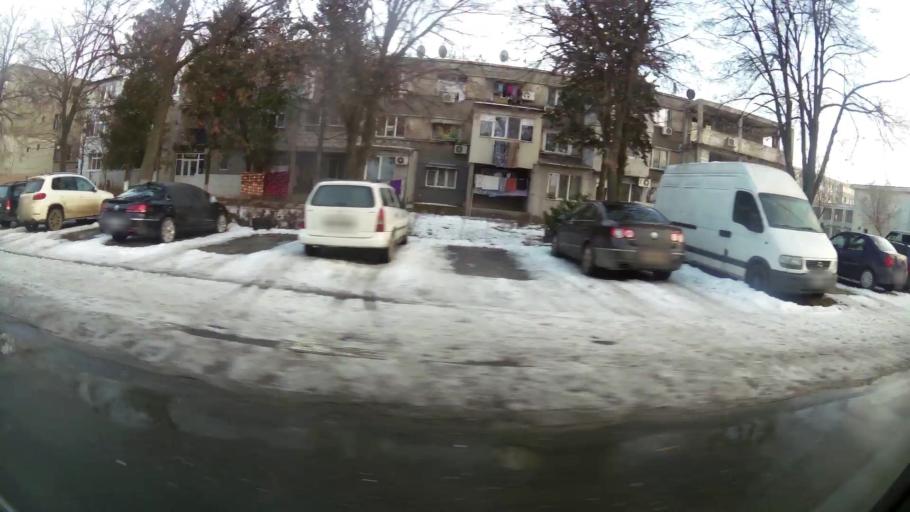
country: RO
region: Ilfov
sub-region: Comuna Popesti-Leordeni
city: Popesti-Leordeni
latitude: 44.3653
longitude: 26.1945
